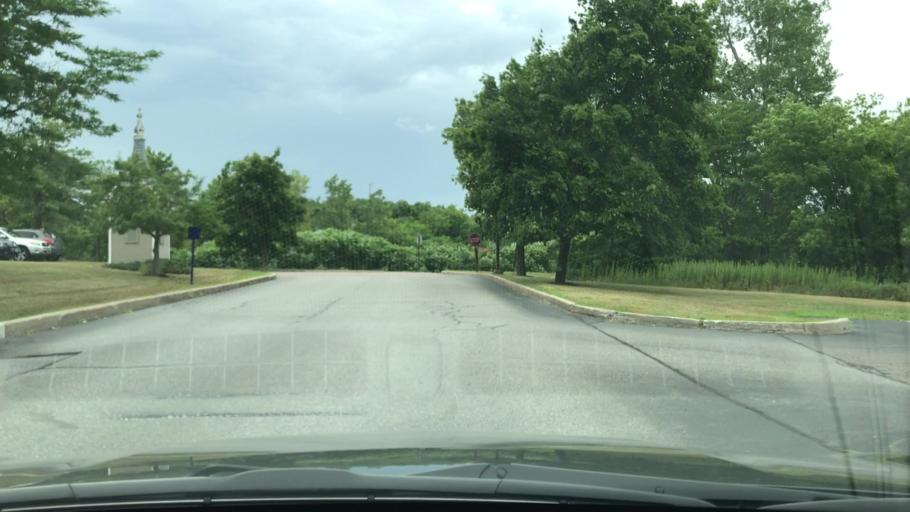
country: US
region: Vermont
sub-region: Chittenden County
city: South Burlington
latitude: 44.4731
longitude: -73.1866
